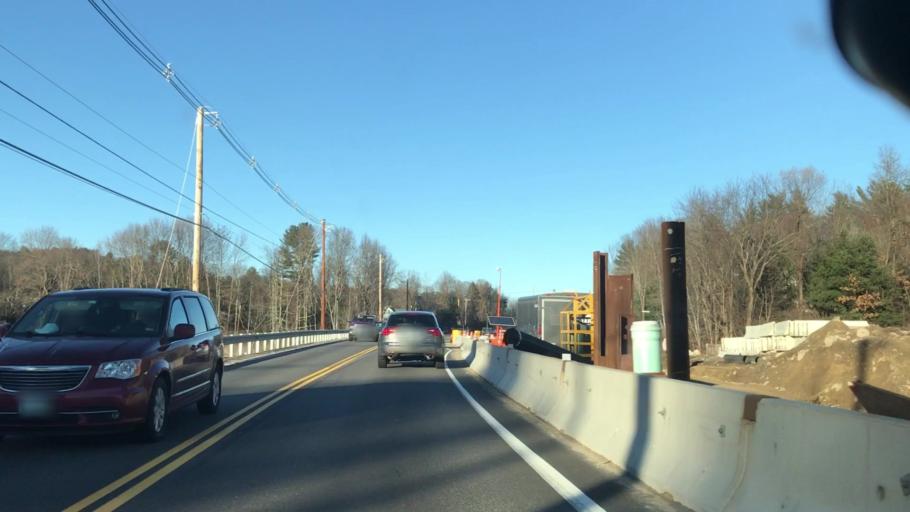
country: US
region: New Hampshire
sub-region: Hillsborough County
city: Bedford
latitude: 42.9494
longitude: -71.5122
